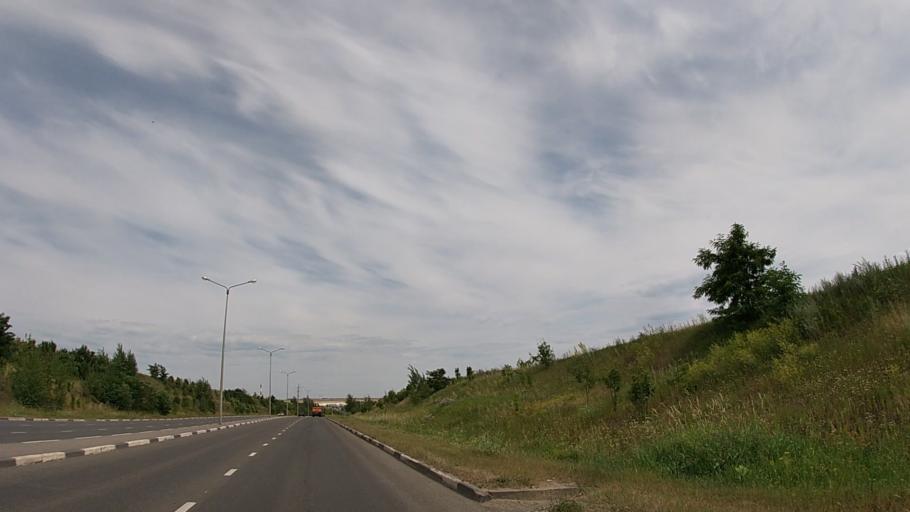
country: RU
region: Belgorod
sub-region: Belgorodskiy Rayon
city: Belgorod
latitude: 50.6015
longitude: 36.5300
